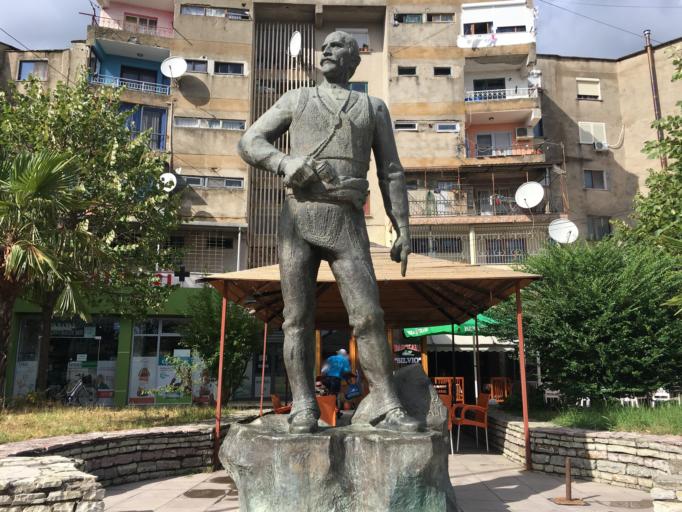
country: AL
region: Shkoder
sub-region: Rrethi i Shkodres
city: Shkoder
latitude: 42.0731
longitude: 19.5210
